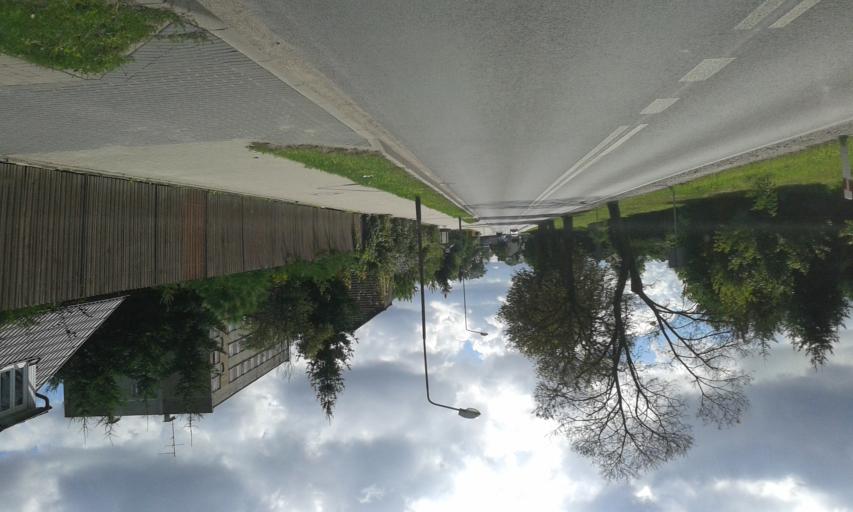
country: PL
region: West Pomeranian Voivodeship
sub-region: Powiat walecki
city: Walcz
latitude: 53.2824
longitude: 16.4625
